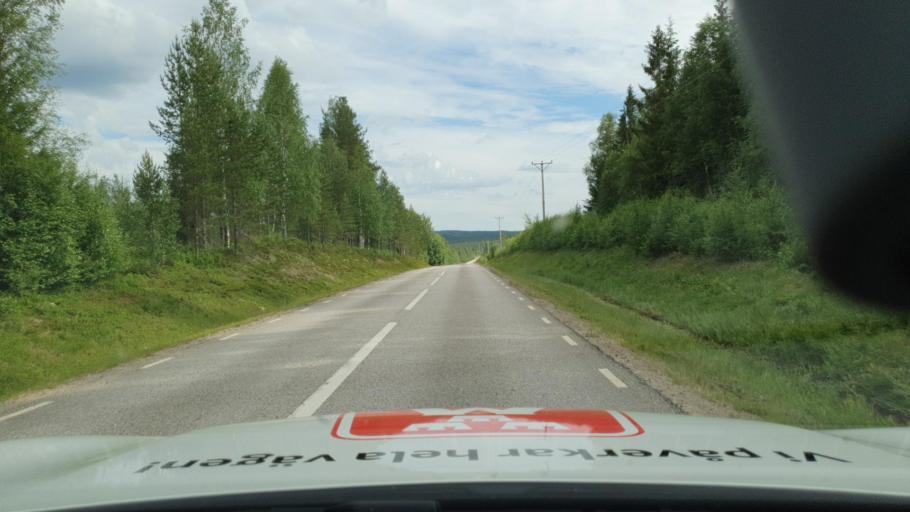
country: NO
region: Hedmark
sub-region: Trysil
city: Innbygda
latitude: 61.0010
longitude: 12.4868
